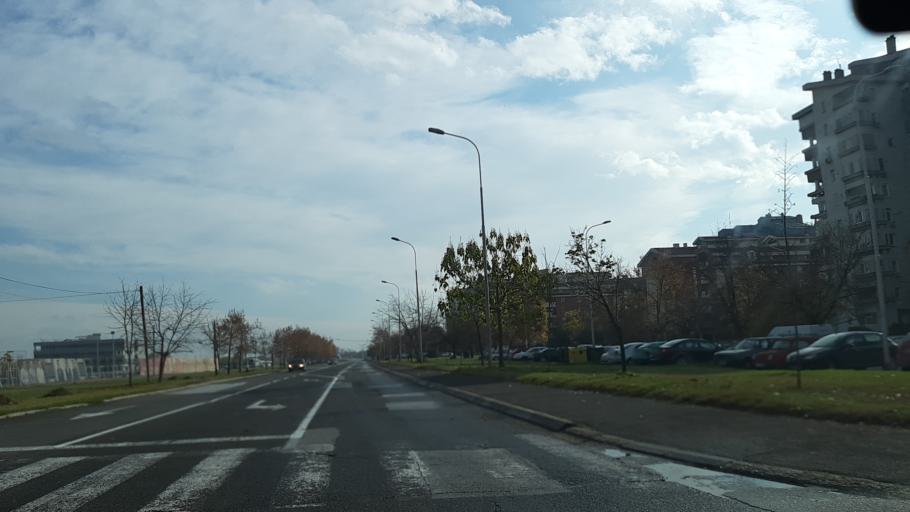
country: MK
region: Kisela Voda
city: Usje
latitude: 41.9879
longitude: 21.4779
